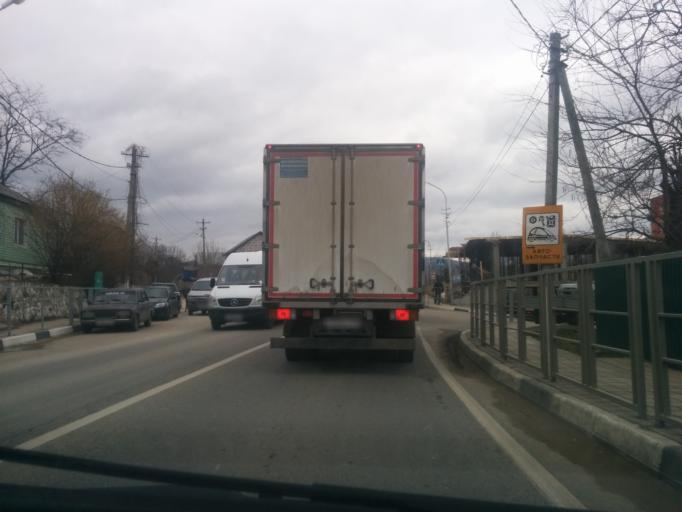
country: RU
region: Krasnodarskiy
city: Novomikhaylovskiy
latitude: 44.2552
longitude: 38.8493
